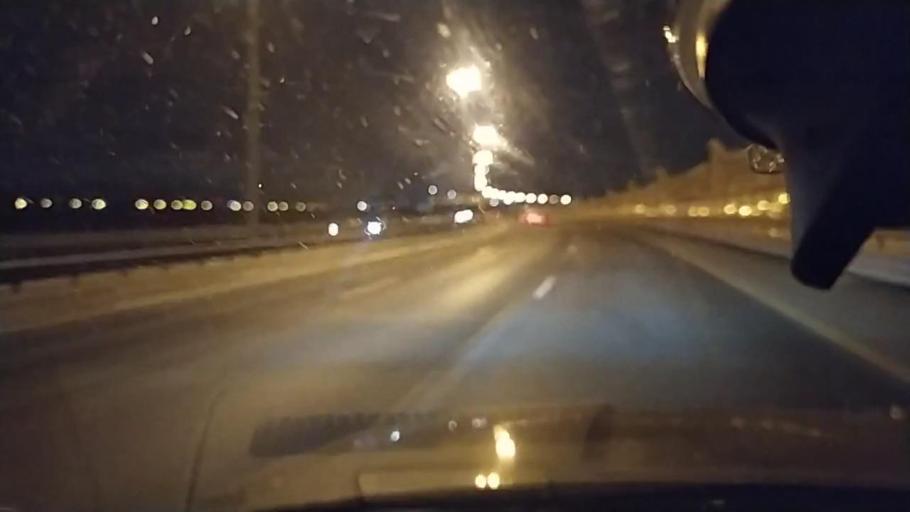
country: RU
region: St.-Petersburg
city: Lakhtinskiy
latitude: 60.0393
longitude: 30.1612
